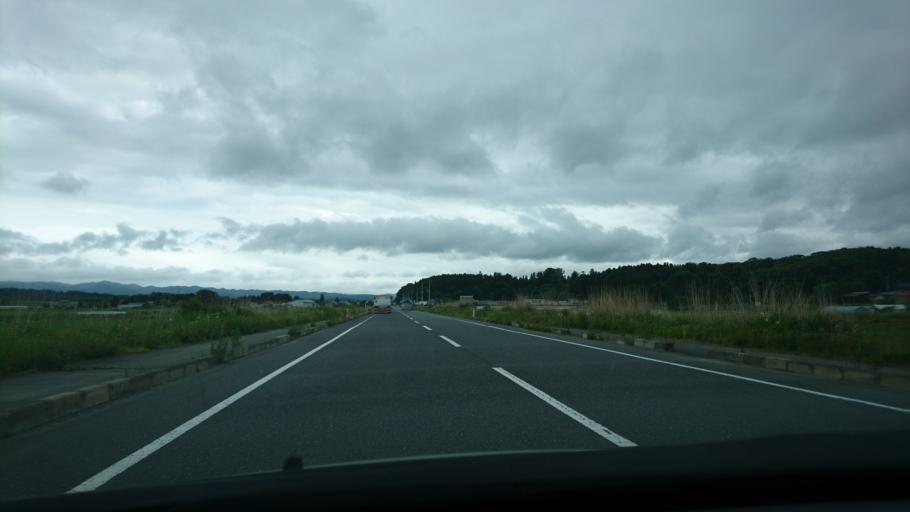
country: JP
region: Iwate
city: Ichinoseki
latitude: 38.7386
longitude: 141.2567
